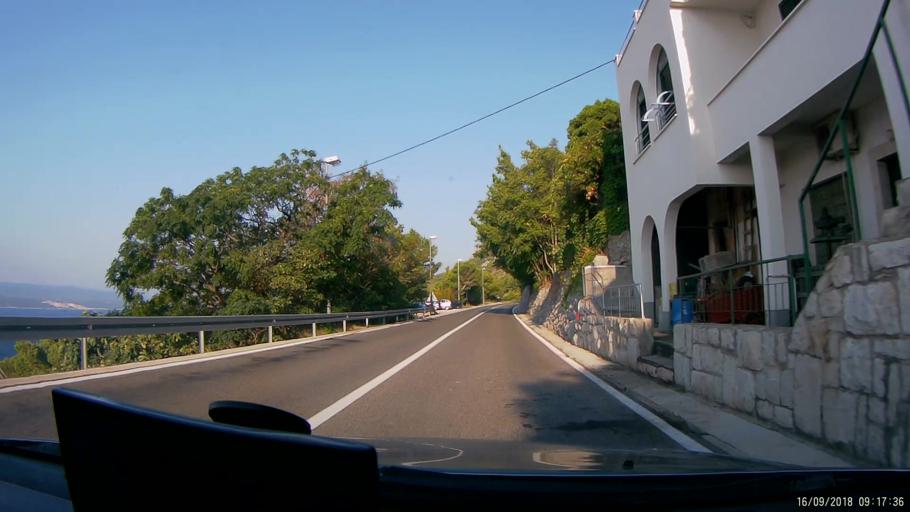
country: HR
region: Splitsko-Dalmatinska
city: Donja Brela
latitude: 43.4025
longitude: 16.8536
